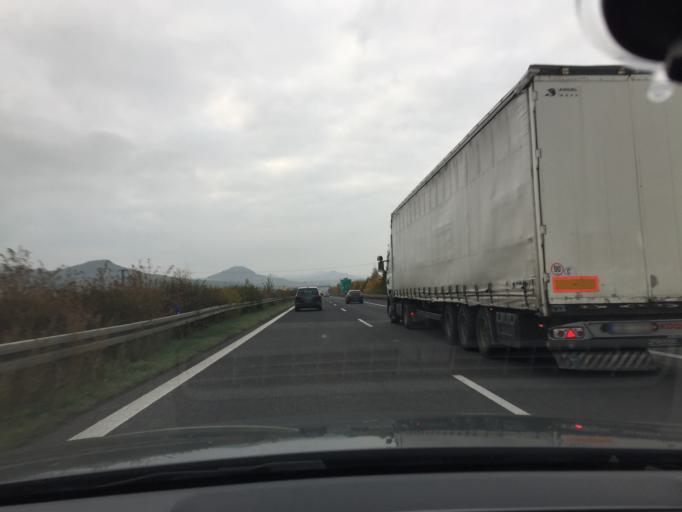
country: CZ
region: Ustecky
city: Lovosice
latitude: 50.5039
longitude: 14.0522
